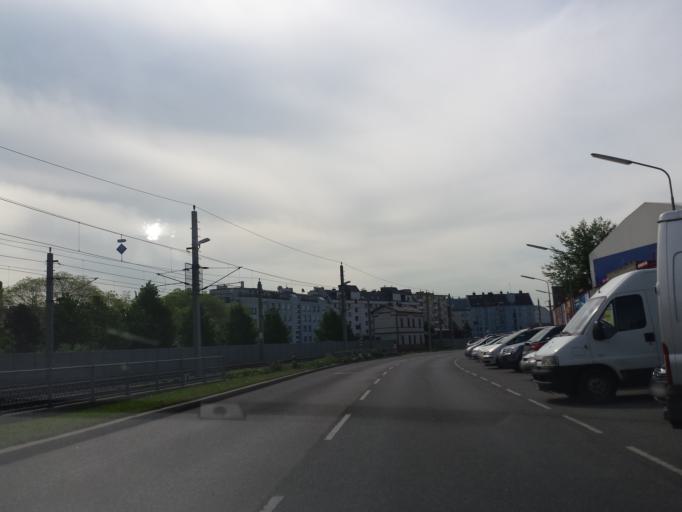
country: AT
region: Vienna
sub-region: Wien Stadt
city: Vienna
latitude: 48.1798
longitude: 16.4074
